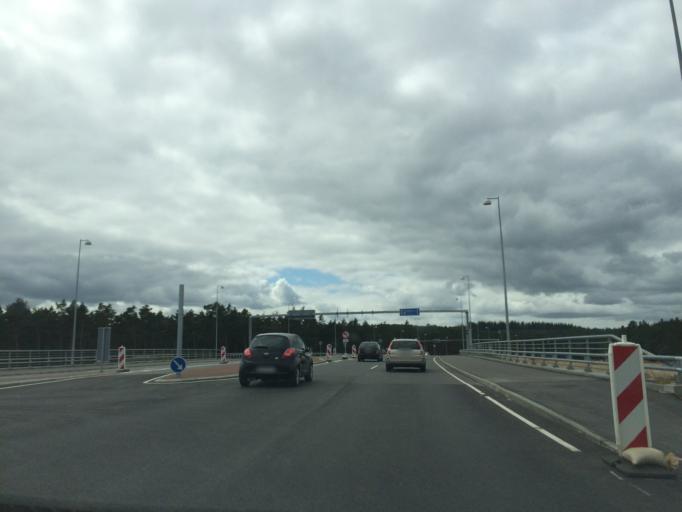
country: DK
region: Central Jutland
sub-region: Silkeborg Kommune
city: Svejbaek
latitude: 56.1694
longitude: 9.6027
